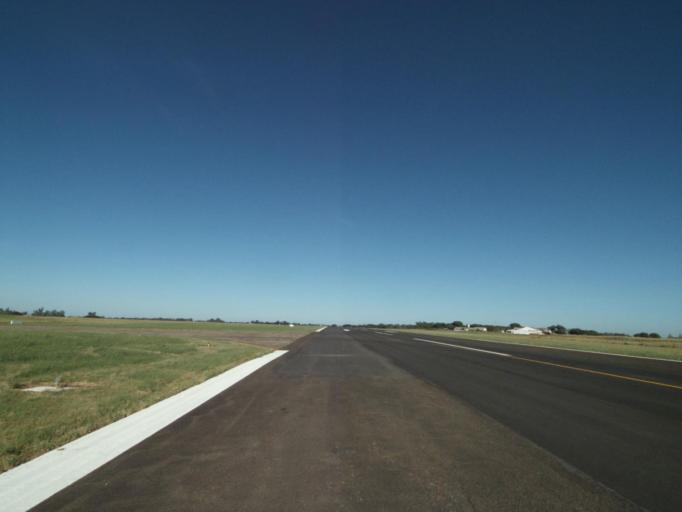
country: BR
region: Rio Grande do Sul
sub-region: Uruguaiana
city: Uruguaiana
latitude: -29.7819
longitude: -57.0351
